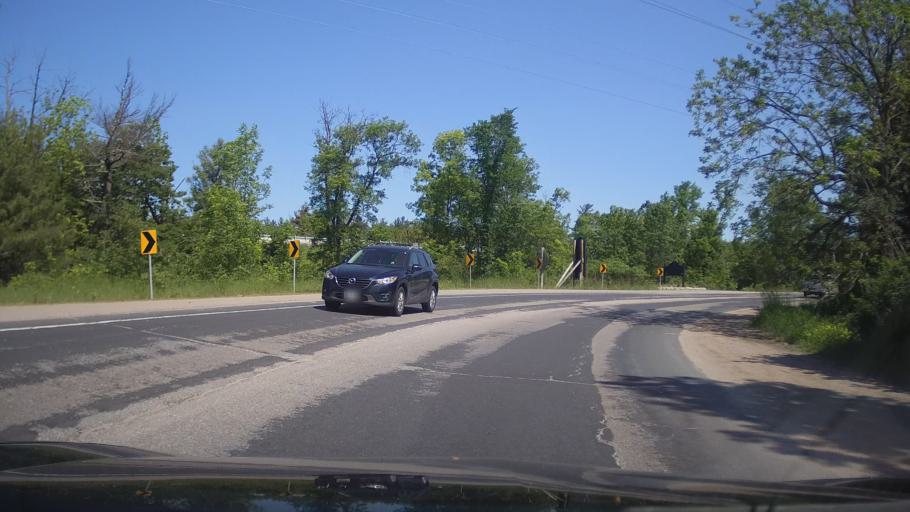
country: CA
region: Ontario
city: Orillia
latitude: 44.7514
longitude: -79.3385
